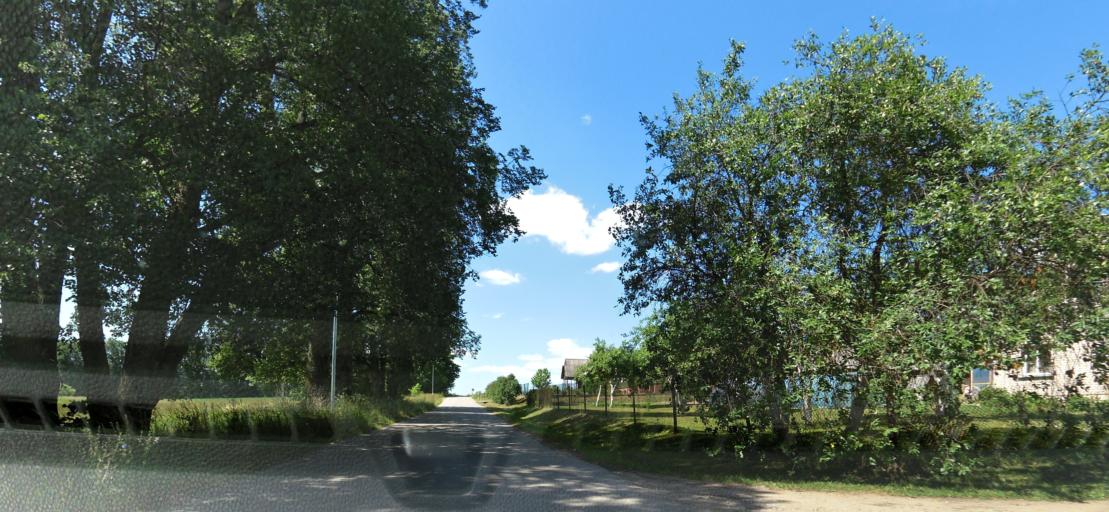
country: LT
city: Nemencine
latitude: 54.8756
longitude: 25.5413
